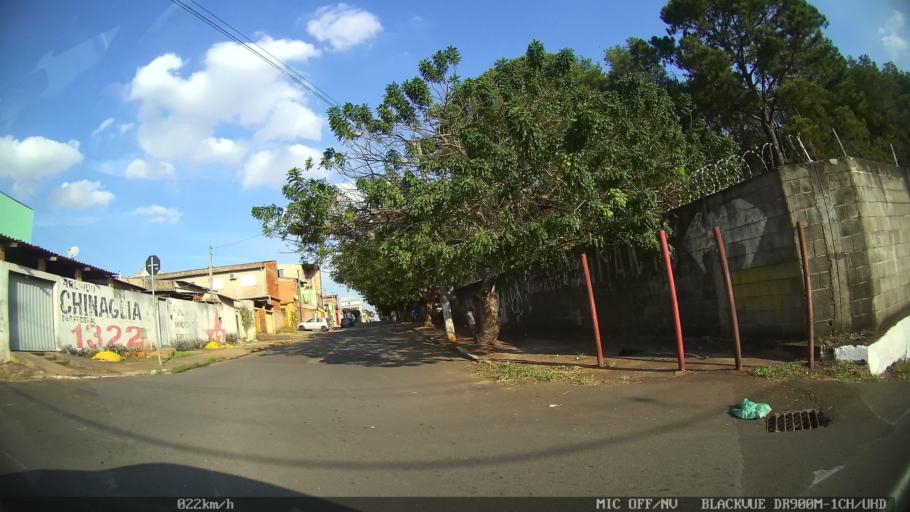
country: BR
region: Sao Paulo
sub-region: Hortolandia
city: Hortolandia
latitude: -22.8744
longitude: -47.1472
